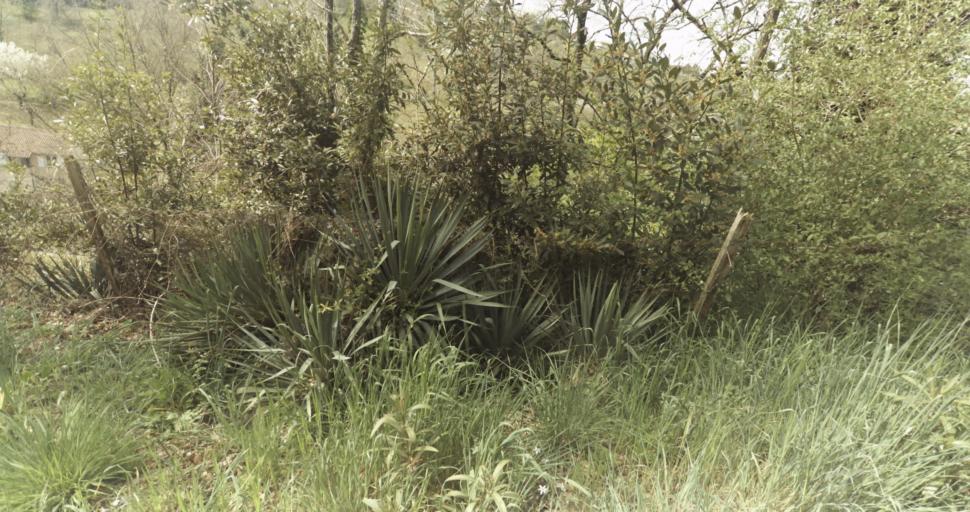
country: FR
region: Midi-Pyrenees
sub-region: Departement du Tarn-et-Garonne
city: Moissac
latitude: 44.1030
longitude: 1.0726
